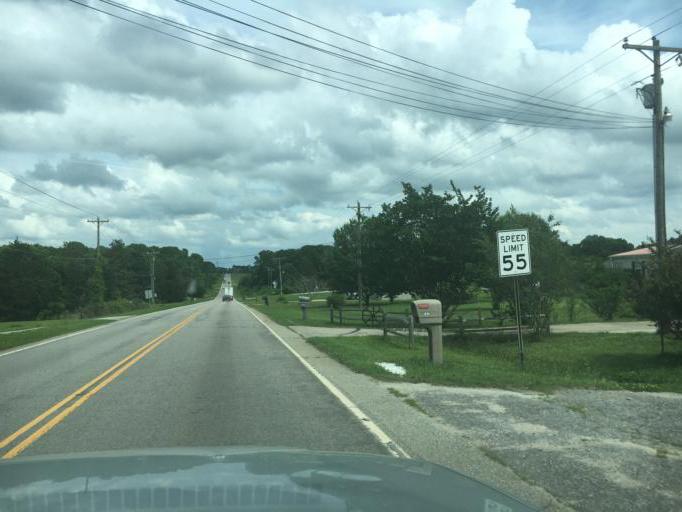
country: US
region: South Carolina
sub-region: Anderson County
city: Williamston
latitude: 34.6339
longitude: -82.4118
